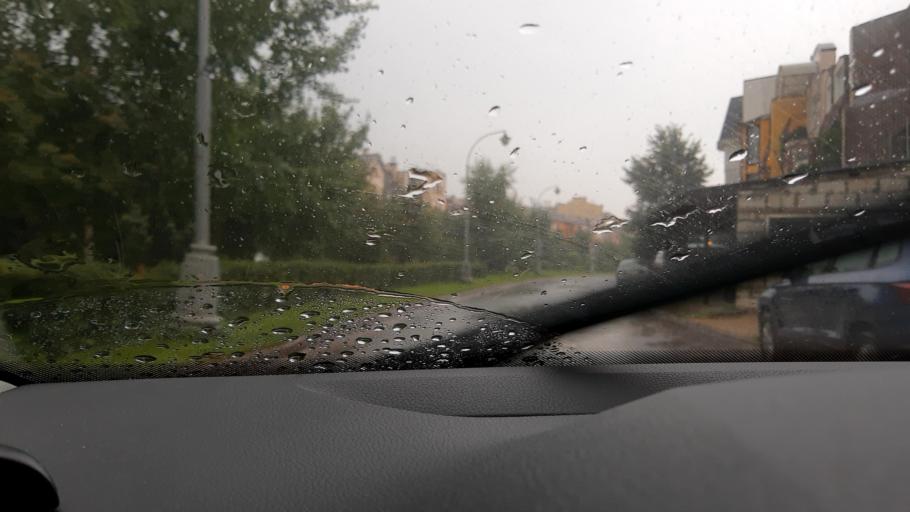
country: RU
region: Moskovskaya
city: Pavshino
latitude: 55.8789
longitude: 37.3645
